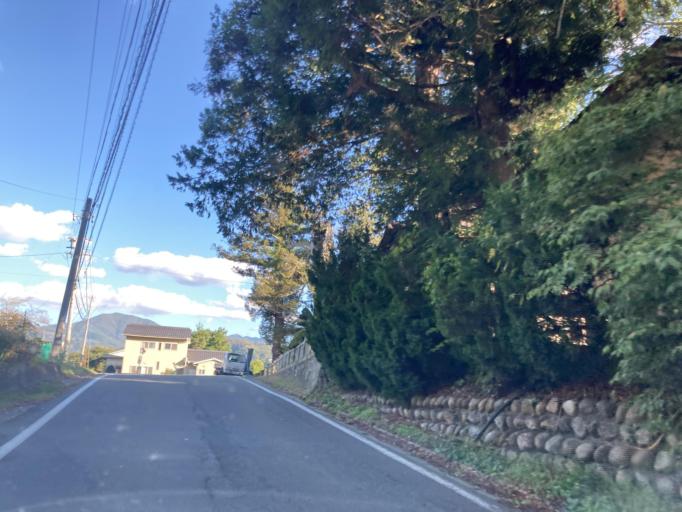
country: JP
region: Nagano
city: Omachi
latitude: 36.4423
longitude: 137.9846
